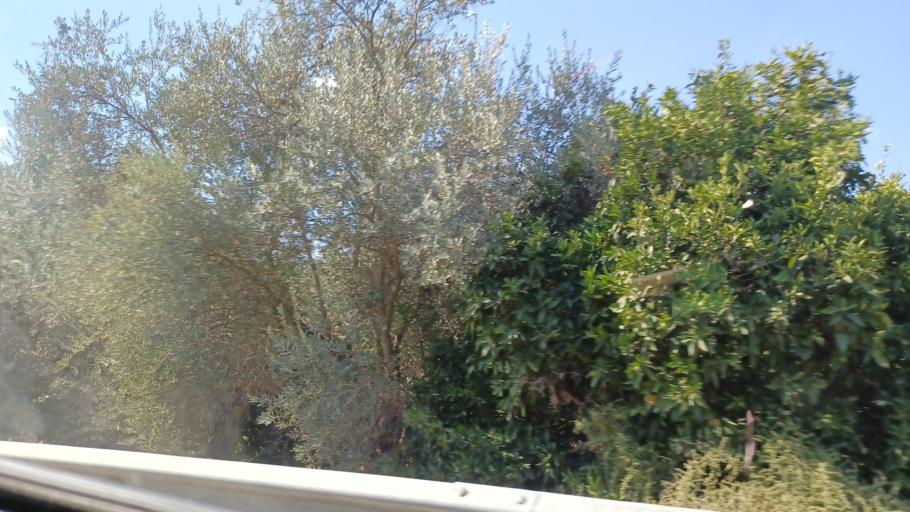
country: CY
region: Pafos
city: Polis
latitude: 34.9954
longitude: 32.4457
